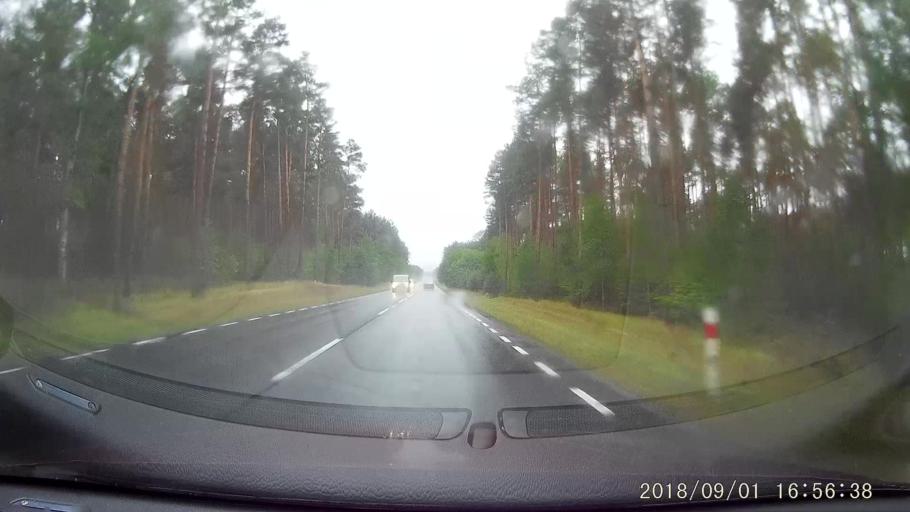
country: PL
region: Lubusz
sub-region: Powiat zielonogorski
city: Swidnica
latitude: 51.9400
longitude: 15.4325
